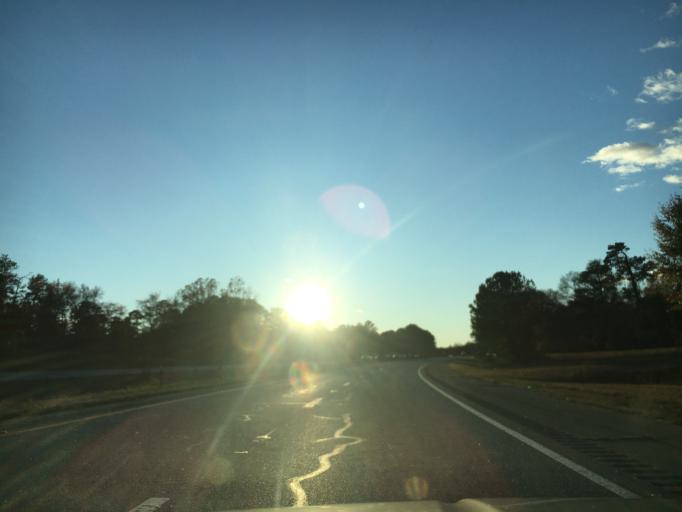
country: US
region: South Carolina
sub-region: Richland County
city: Columbia
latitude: 34.0354
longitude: -81.0237
